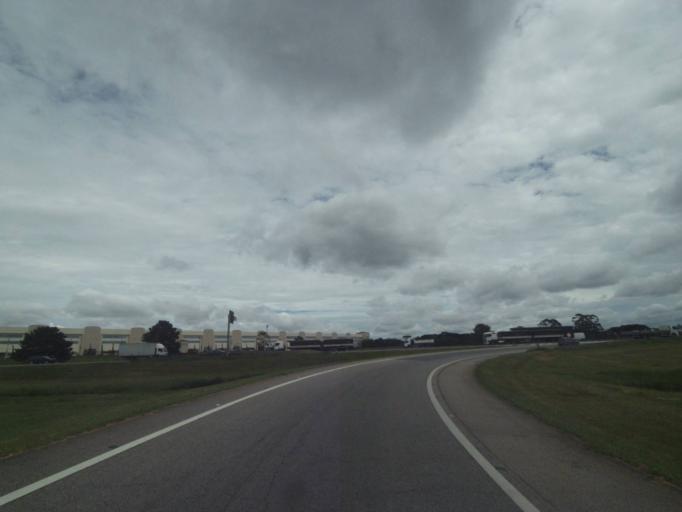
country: BR
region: Parana
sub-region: Sao Jose Dos Pinhais
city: Sao Jose dos Pinhais
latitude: -25.5134
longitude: -49.1283
